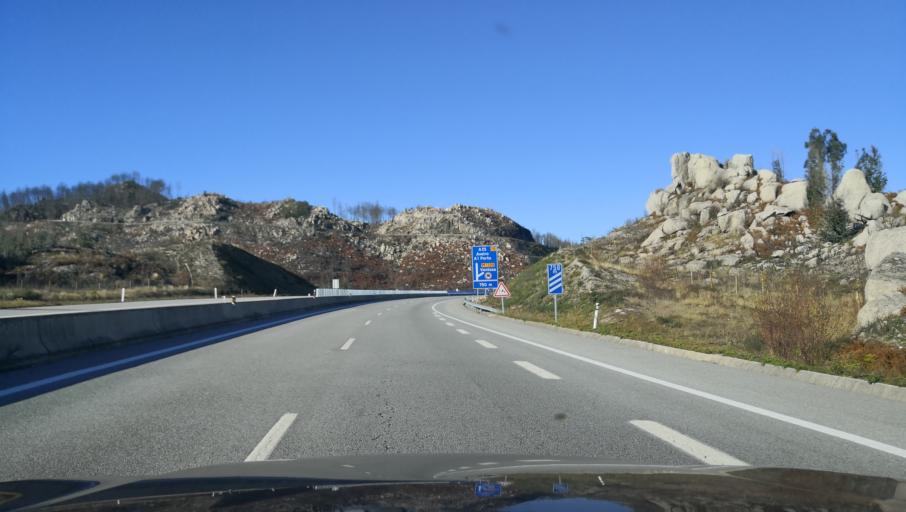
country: PT
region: Viseu
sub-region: Vouzela
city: Vouzela
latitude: 40.6855
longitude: -8.0772
